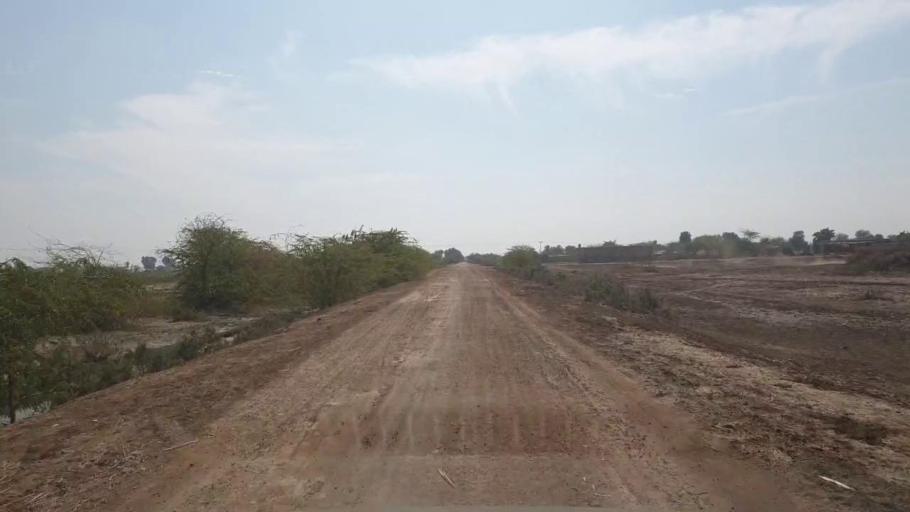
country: PK
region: Sindh
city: Mirwah Gorchani
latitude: 25.4355
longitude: 69.1960
